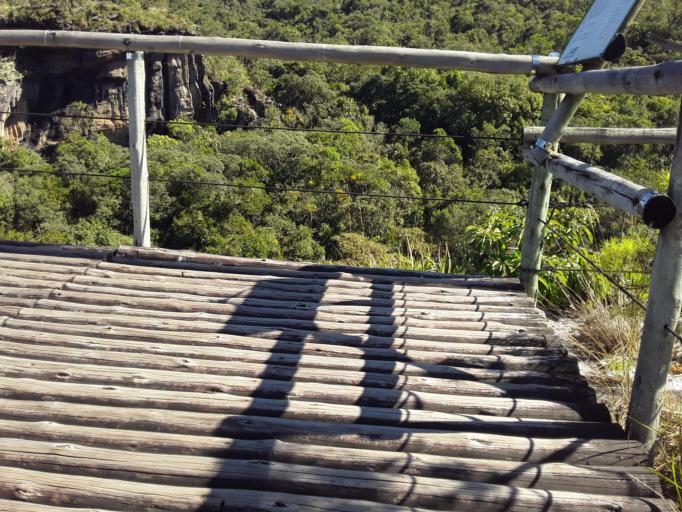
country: BR
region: Minas Gerais
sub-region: Lima Duarte
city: Lima Duarte
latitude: -21.7144
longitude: -43.8936
